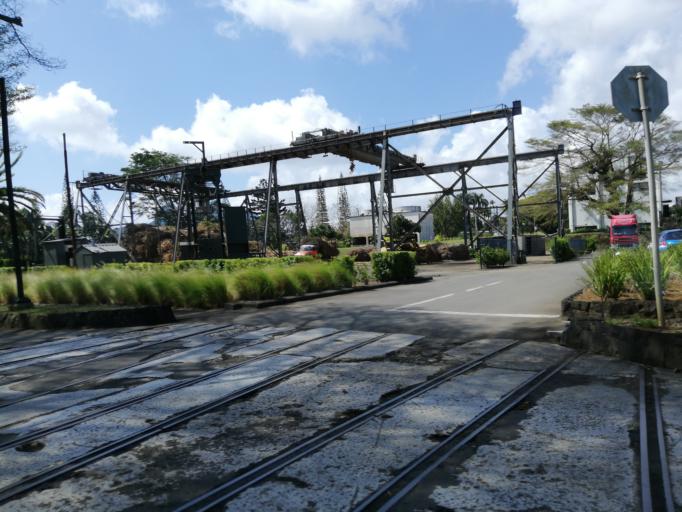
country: MU
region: Moka
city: Verdun
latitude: -20.2245
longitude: 57.5330
